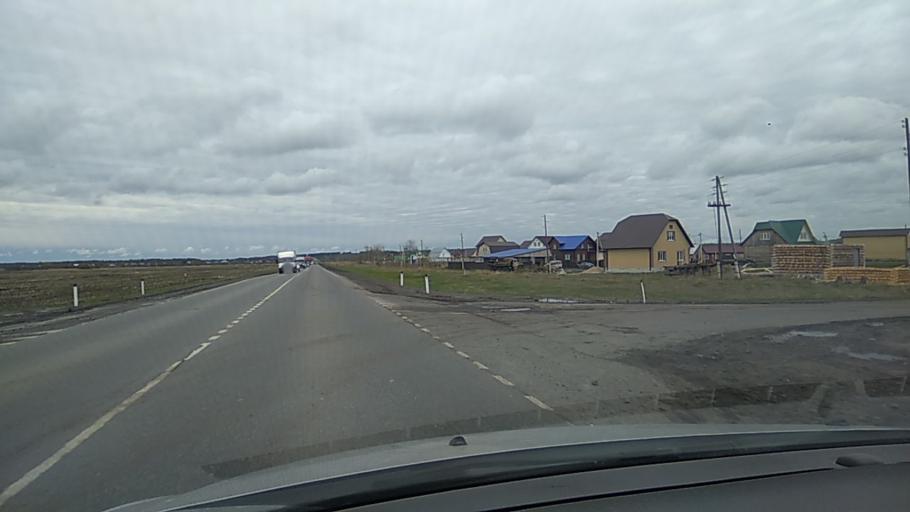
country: RU
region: Tjumen
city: Chervishevo
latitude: 56.9251
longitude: 65.4245
